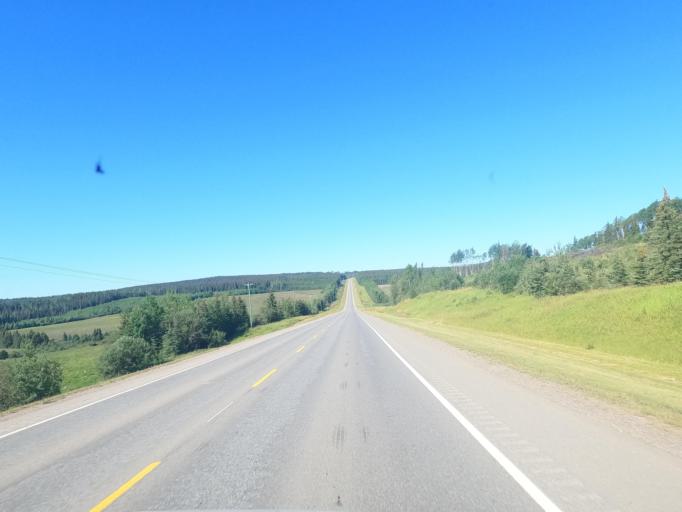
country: CA
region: British Columbia
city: Fort St. John
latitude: 56.6296
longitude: -121.5353
